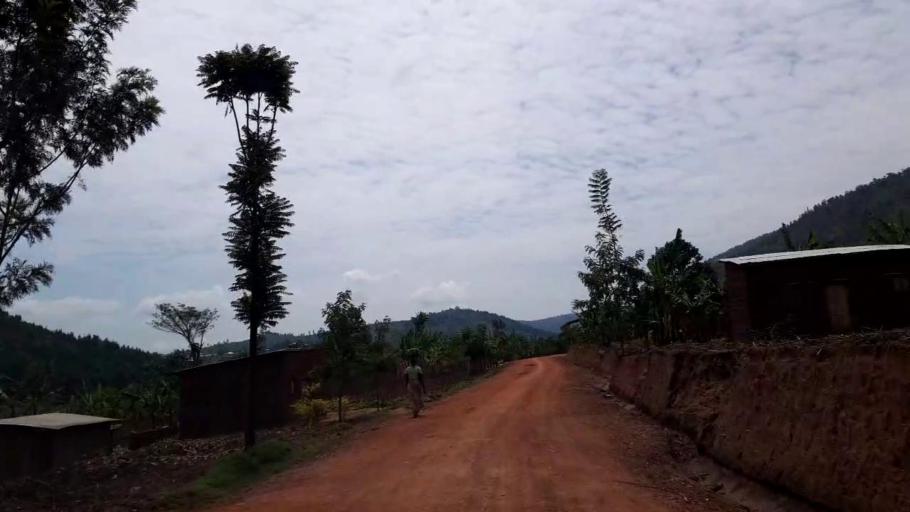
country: RW
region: Northern Province
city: Byumba
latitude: -1.5056
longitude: 30.1941
